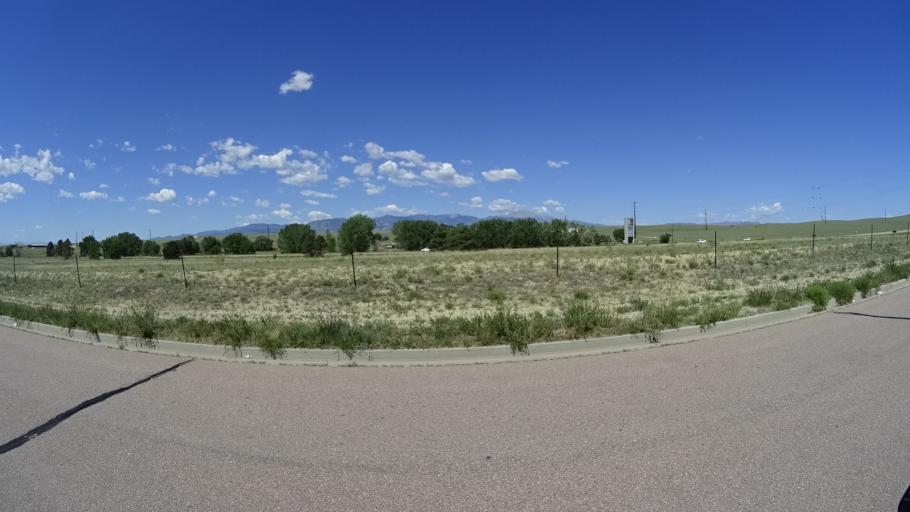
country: US
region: Colorado
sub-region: El Paso County
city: Security-Widefield
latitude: 38.7797
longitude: -104.6575
